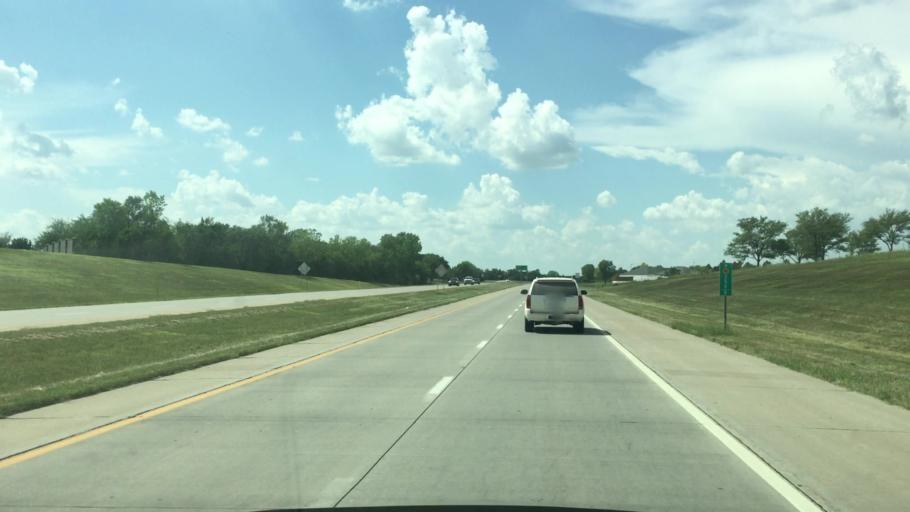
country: US
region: Kansas
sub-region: Butler County
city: Andover
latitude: 37.6965
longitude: -97.1906
